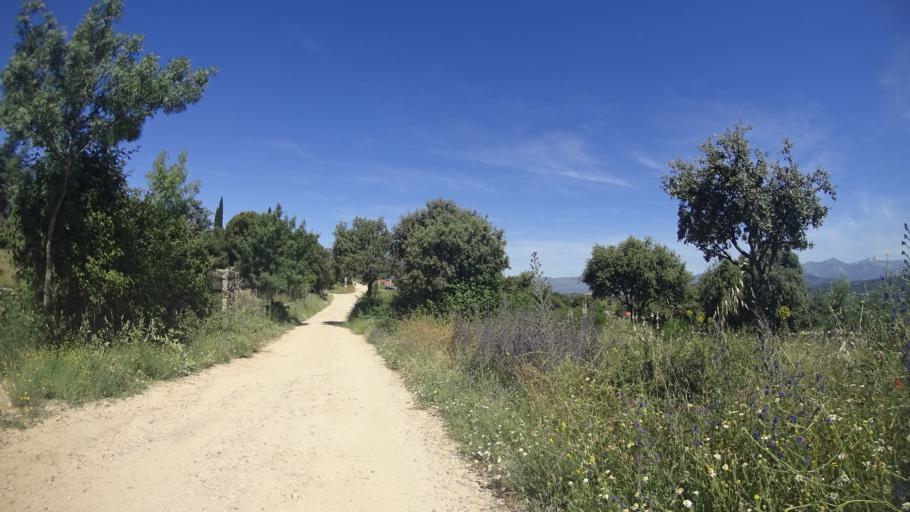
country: ES
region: Madrid
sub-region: Provincia de Madrid
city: Galapagar
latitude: 40.5970
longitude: -3.9971
